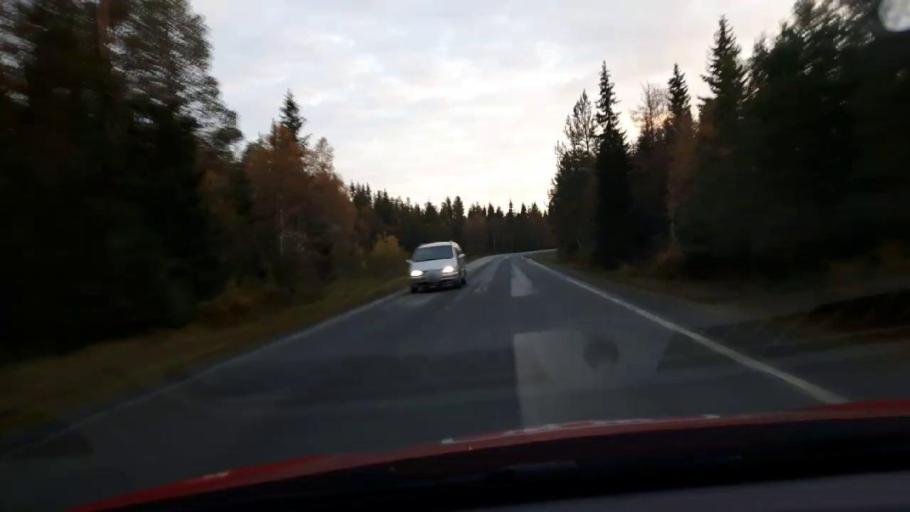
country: SE
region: Jaemtland
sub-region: OEstersunds Kommun
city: Ostersund
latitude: 63.2718
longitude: 14.6255
